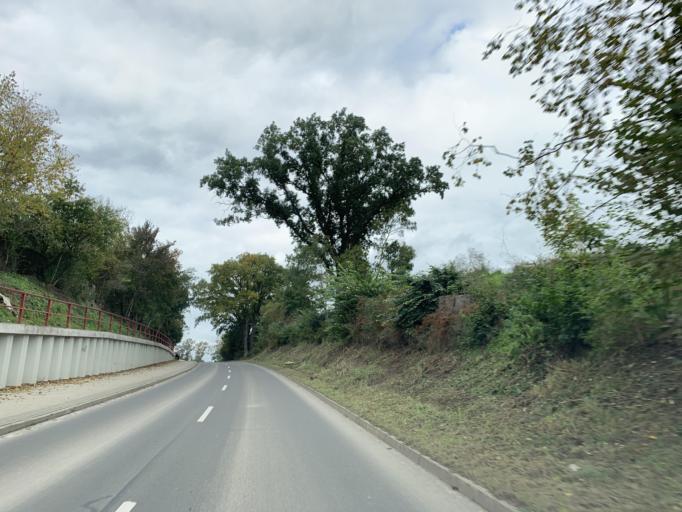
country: DE
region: Mecklenburg-Vorpommern
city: Blankensee
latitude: 53.4156
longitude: 13.2637
